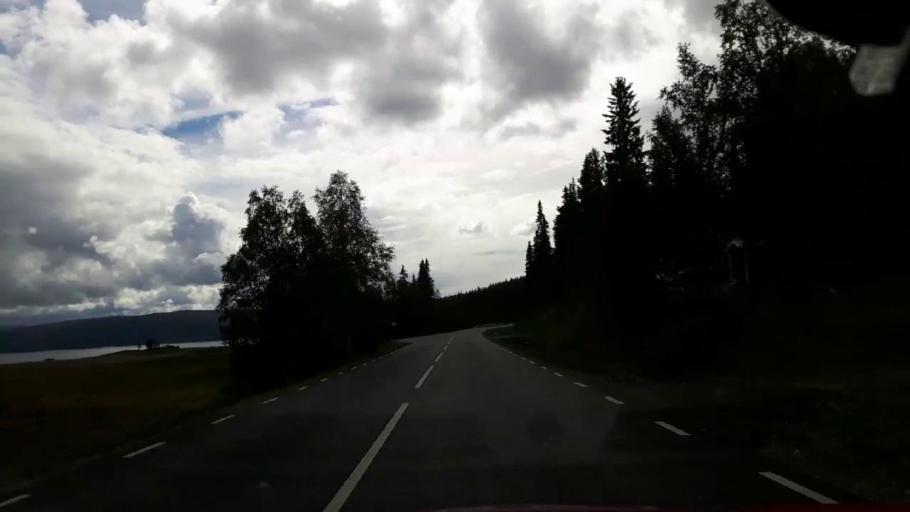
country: NO
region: Nord-Trondelag
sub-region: Royrvik
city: Royrvik
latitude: 64.8189
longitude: 14.0613
